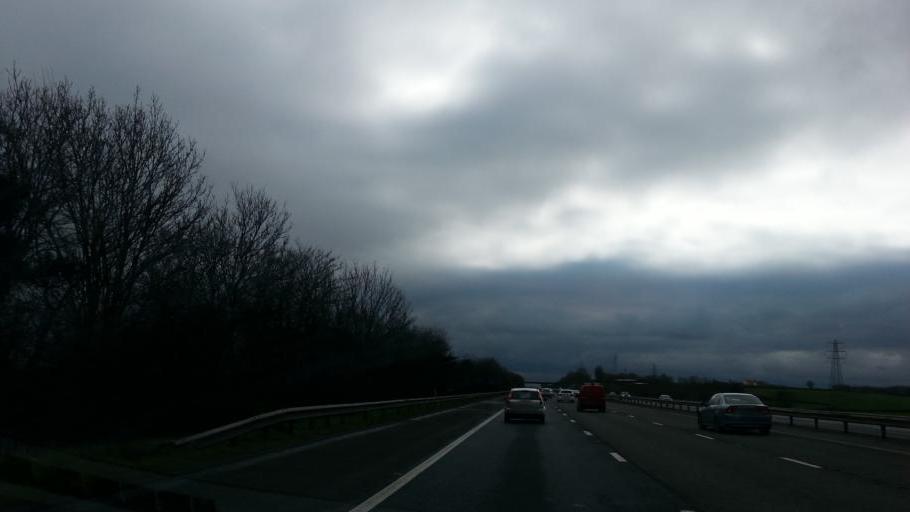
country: GB
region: England
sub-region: Somerset
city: North Petherton
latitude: 51.0748
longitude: -3.0113
